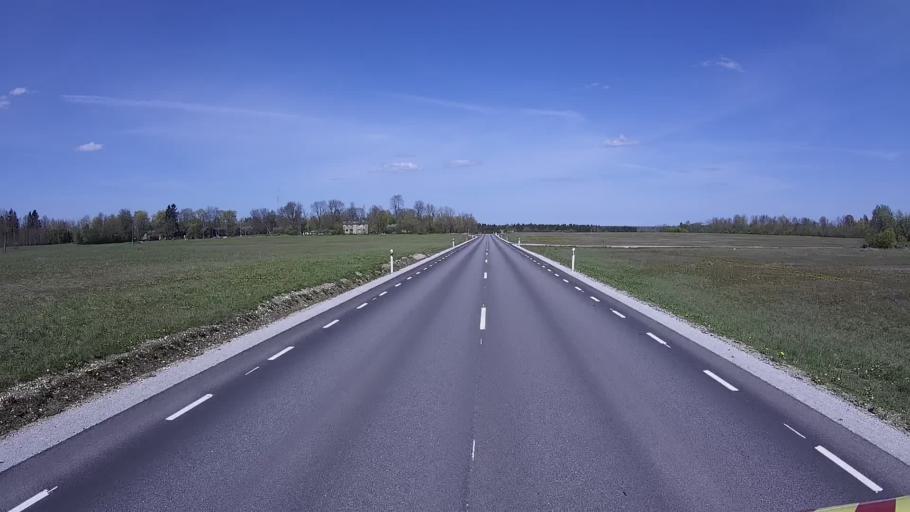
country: EE
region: Harju
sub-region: Paldiski linn
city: Paldiski
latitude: 59.2070
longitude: 24.0955
